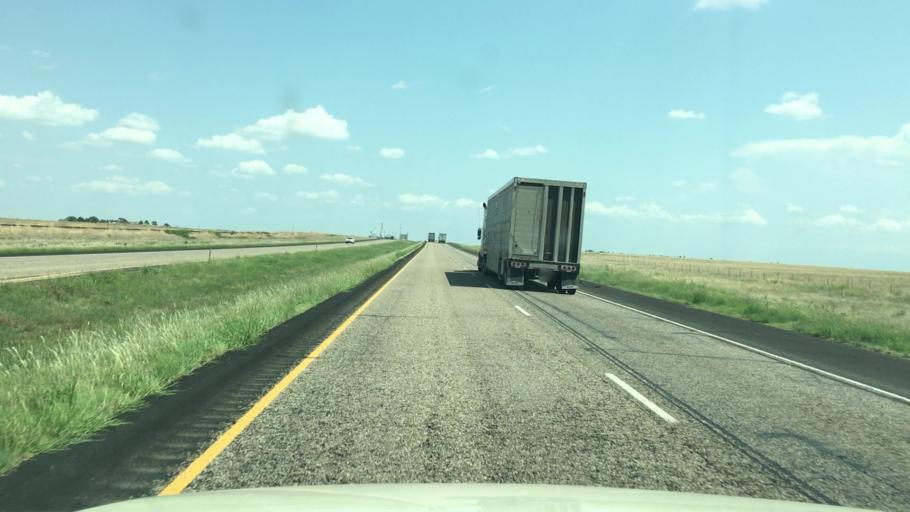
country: US
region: Texas
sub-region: Armstrong County
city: Claude
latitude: 35.1253
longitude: -101.3969
